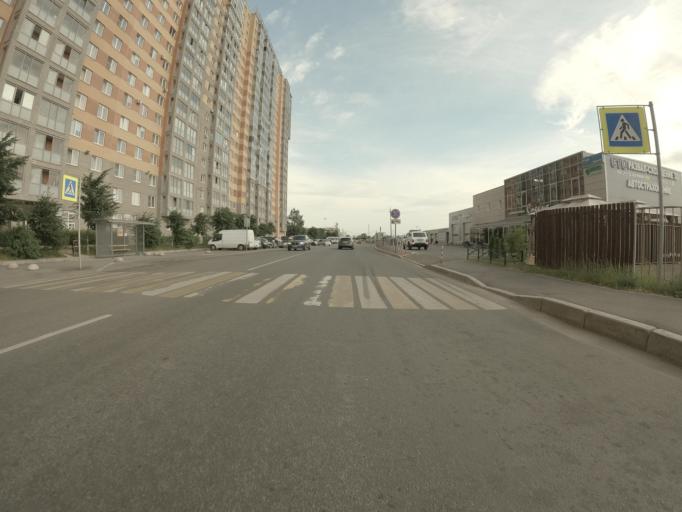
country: RU
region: St.-Petersburg
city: Krasnogvargeisky
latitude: 59.9159
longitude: 30.5043
